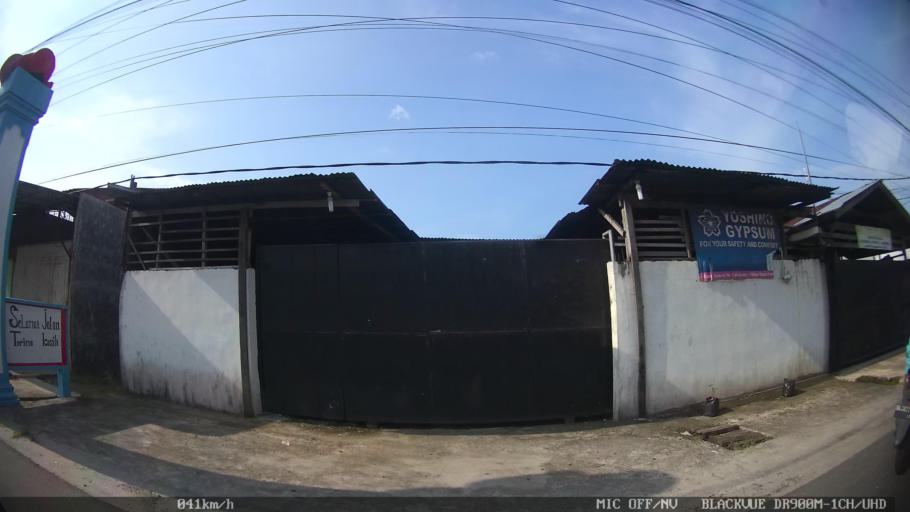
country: ID
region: North Sumatra
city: Percut
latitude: 3.5940
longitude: 98.7722
